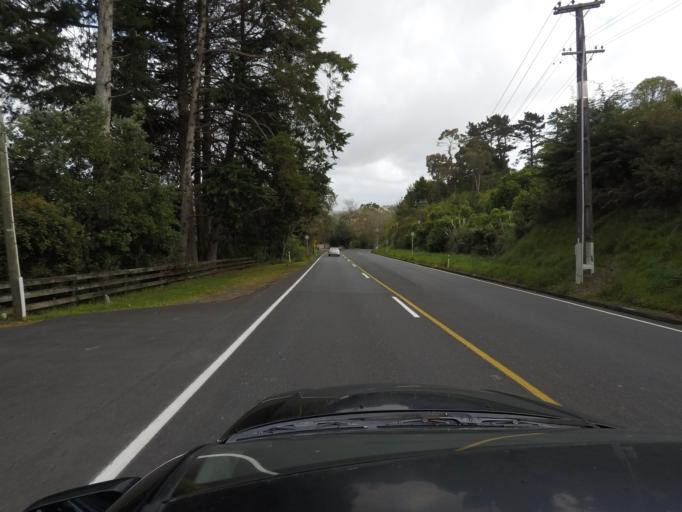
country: NZ
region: Auckland
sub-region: Auckland
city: Pakuranga
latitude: -36.9226
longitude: 174.9333
